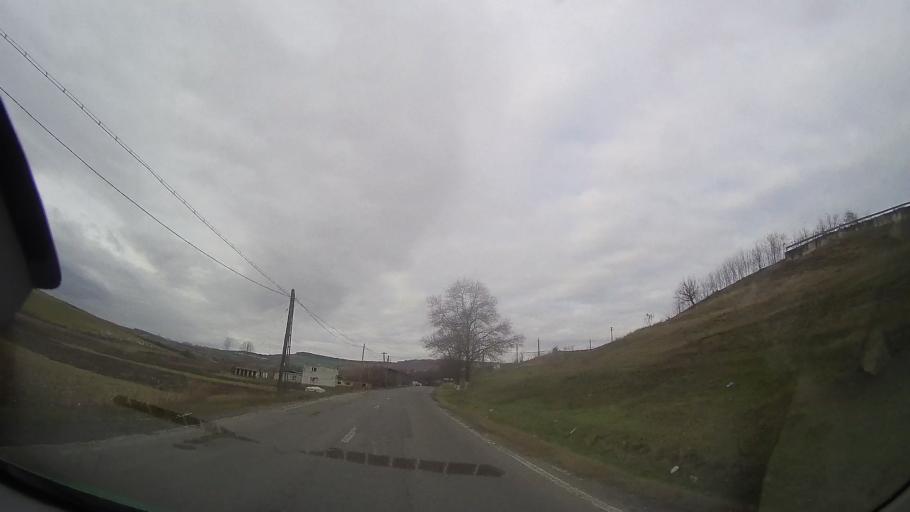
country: RO
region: Bistrita-Nasaud
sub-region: Comuna Urmenis
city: Urmenis
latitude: 46.7653
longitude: 24.3727
